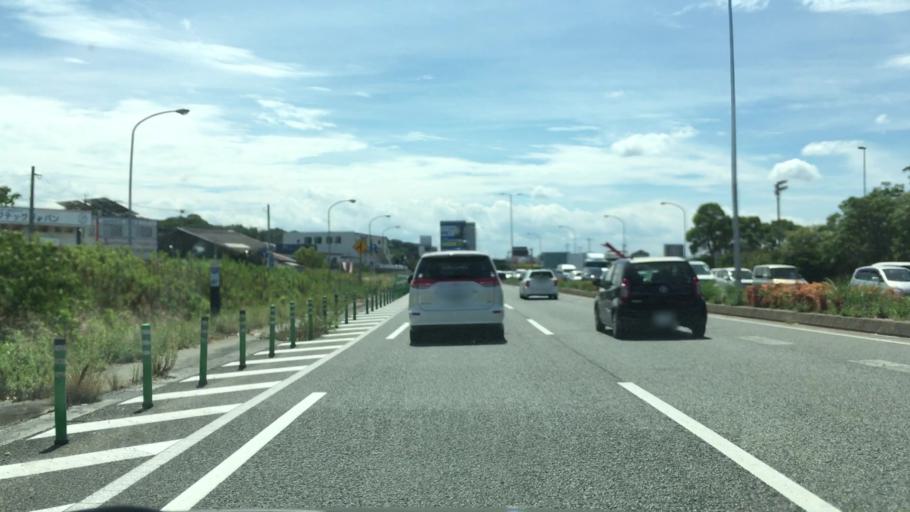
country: JP
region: Fukuoka
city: Onojo
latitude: 33.5305
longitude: 130.4924
